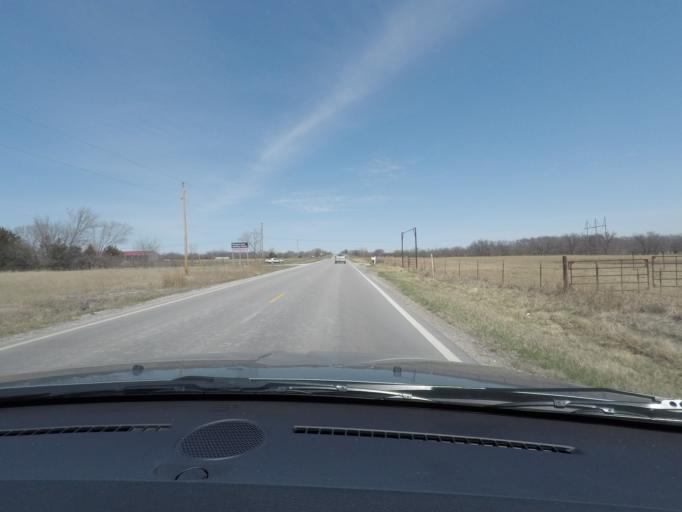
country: US
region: Kansas
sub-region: Lyon County
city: Emporia
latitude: 38.4806
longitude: -96.1710
